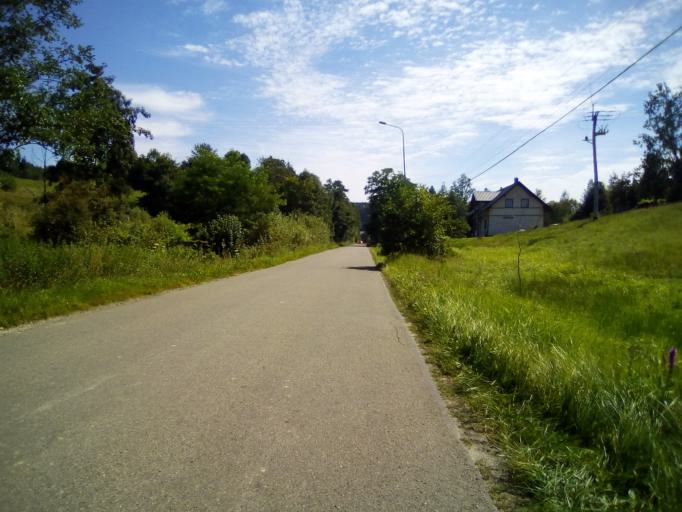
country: PL
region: Subcarpathian Voivodeship
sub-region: Powiat strzyzowski
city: Konieczkowa
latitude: 49.8356
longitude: 21.9308
